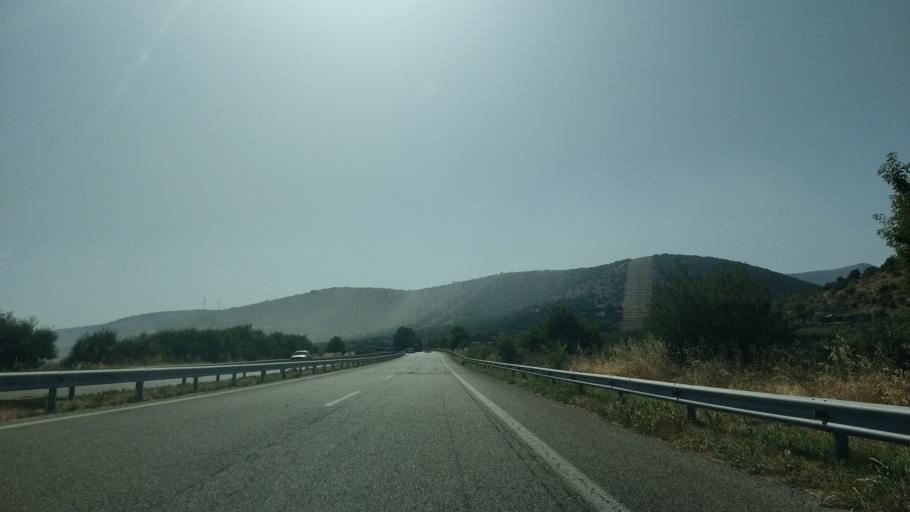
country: GR
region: East Macedonia and Thrace
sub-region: Nomos Kavalas
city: Nea Karvali
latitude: 40.9704
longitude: 24.4974
